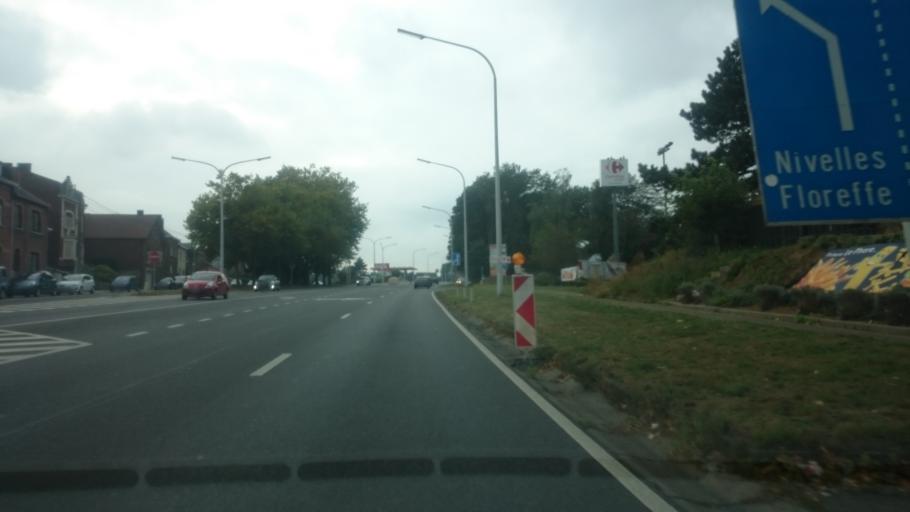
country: BE
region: Wallonia
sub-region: Province de Namur
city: Namur
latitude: 50.4726
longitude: 4.8175
